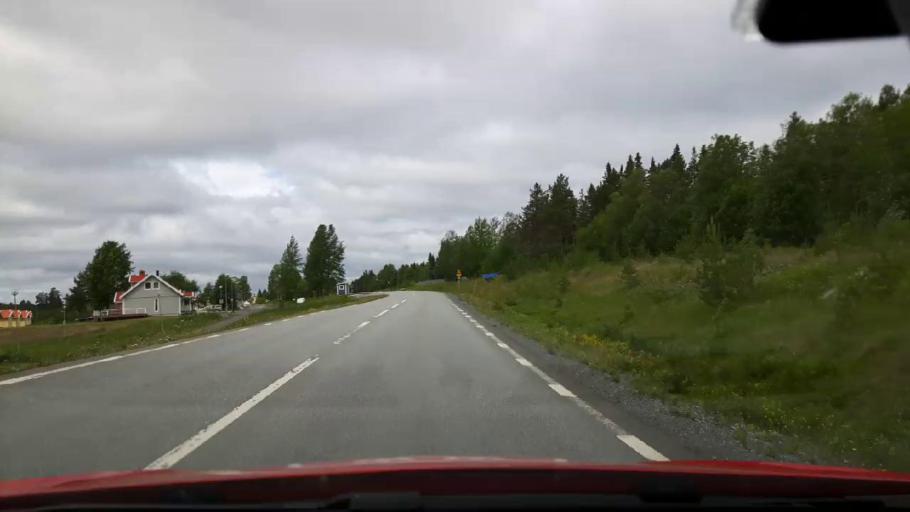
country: SE
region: Jaemtland
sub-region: Krokoms Kommun
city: Krokom
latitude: 63.2898
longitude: 14.4952
